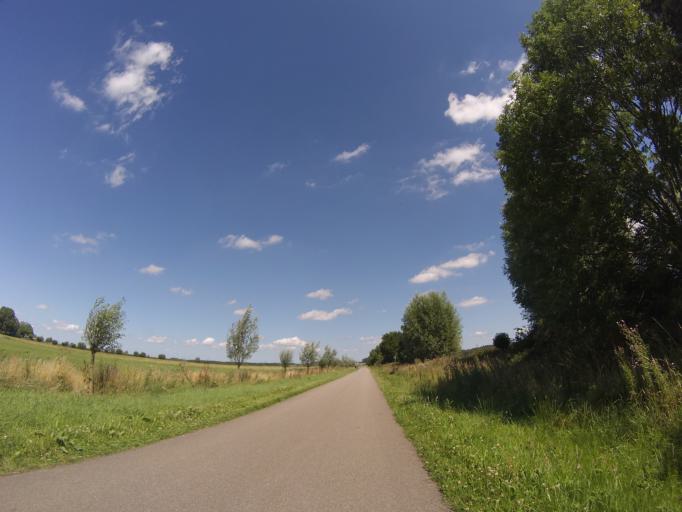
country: NL
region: Utrecht
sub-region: Stichtse Vecht
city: Spechtenkamp
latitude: 52.1271
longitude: 5.0014
